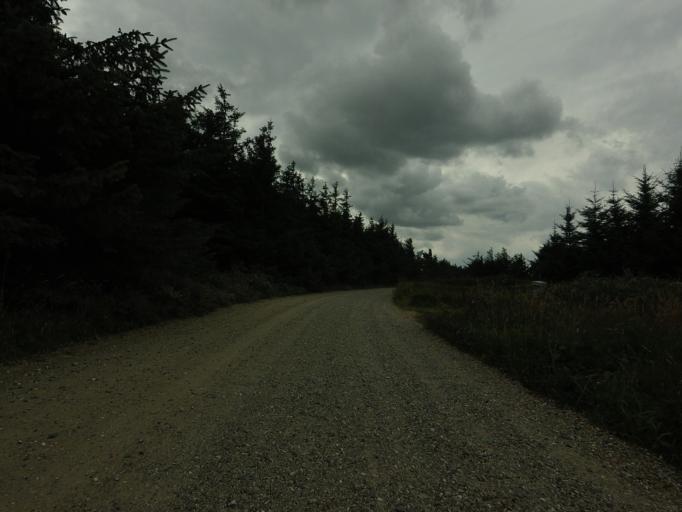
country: DK
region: North Denmark
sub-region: Jammerbugt Kommune
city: Pandrup
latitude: 57.3363
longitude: 9.6816
